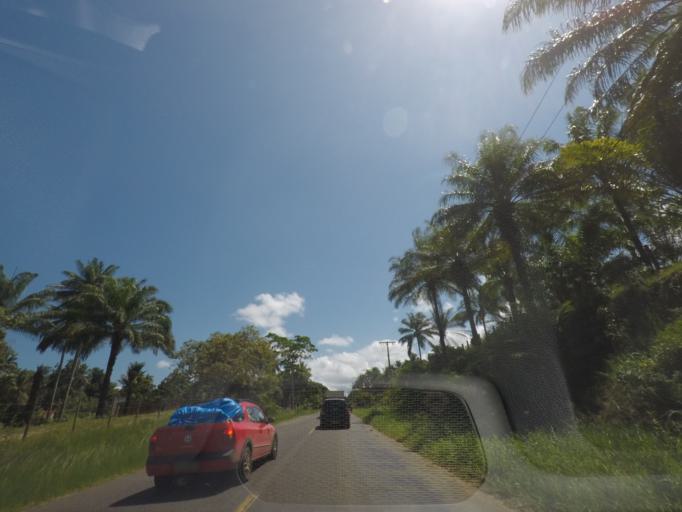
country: BR
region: Bahia
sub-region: Taperoa
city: Taperoa
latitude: -13.4565
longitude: -39.0881
